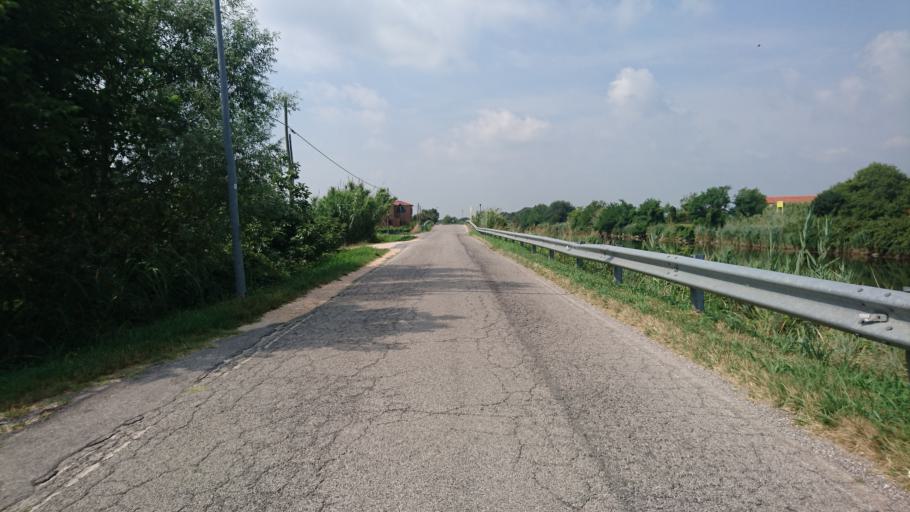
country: IT
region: Veneto
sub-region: Provincia di Venezia
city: Sant'Anna
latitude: 45.1501
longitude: 12.2626
